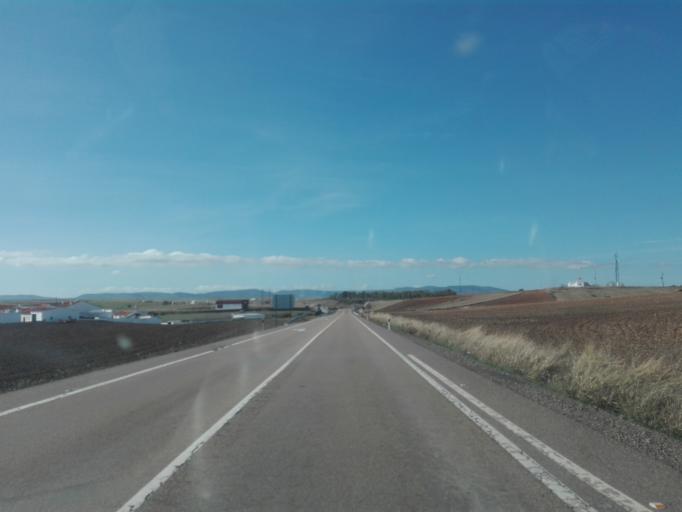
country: ES
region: Extremadura
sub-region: Provincia de Badajoz
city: Ahillones
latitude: 38.2627
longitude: -5.8665
